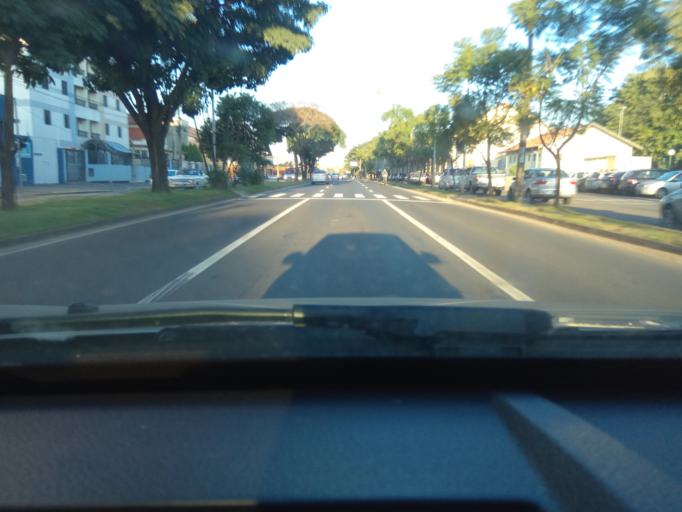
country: BR
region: Sao Paulo
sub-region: Piracicaba
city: Piracicaba
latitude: -22.7356
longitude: -47.6547
